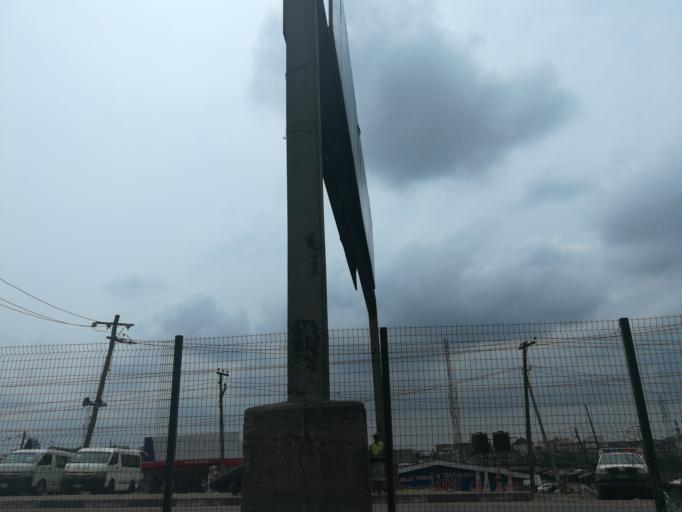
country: NG
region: Lagos
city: Ojota
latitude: 6.5826
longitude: 3.3751
